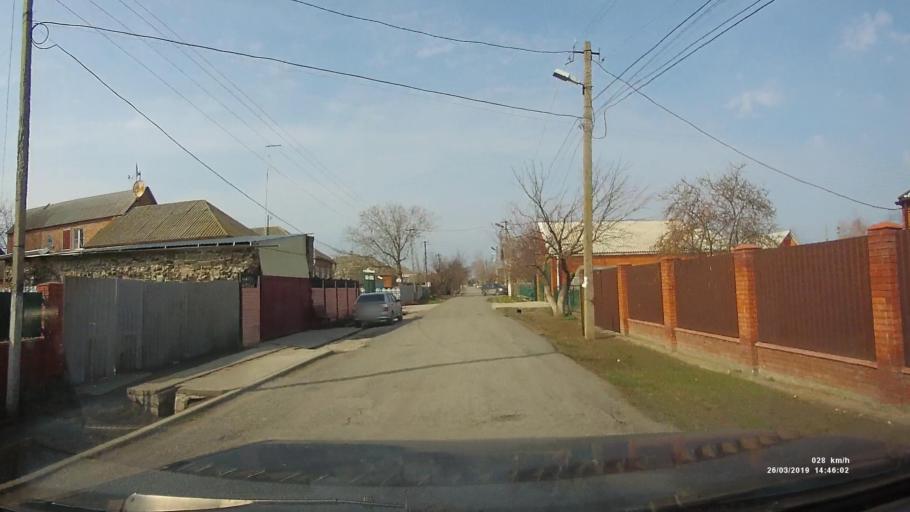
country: RU
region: Rostov
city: Novobessergenovka
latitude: 47.1848
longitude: 38.8609
